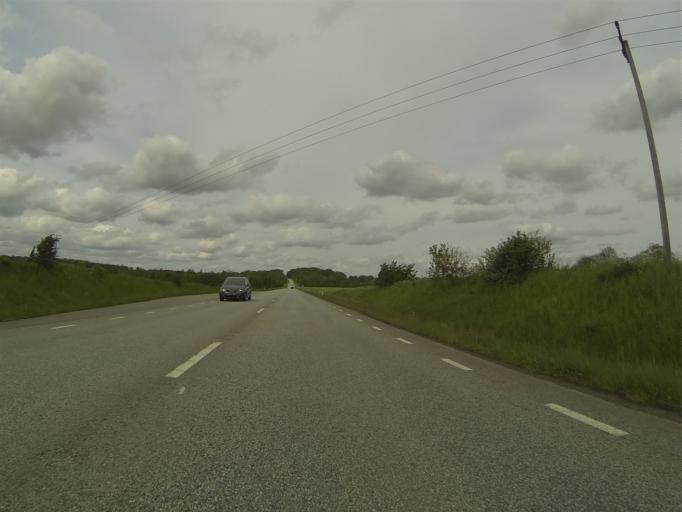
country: SE
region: Skane
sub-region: Sjobo Kommun
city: Sjoebo
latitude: 55.6489
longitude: 13.6943
